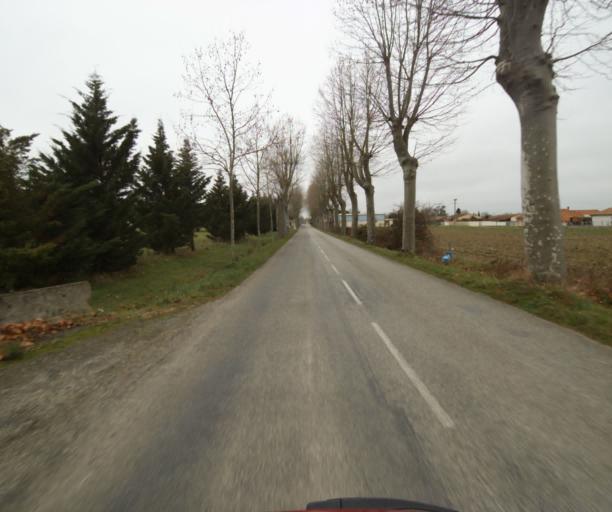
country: FR
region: Midi-Pyrenees
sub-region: Departement de la Haute-Garonne
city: Gaillac-Toulza
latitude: 43.2730
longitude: 1.5068
